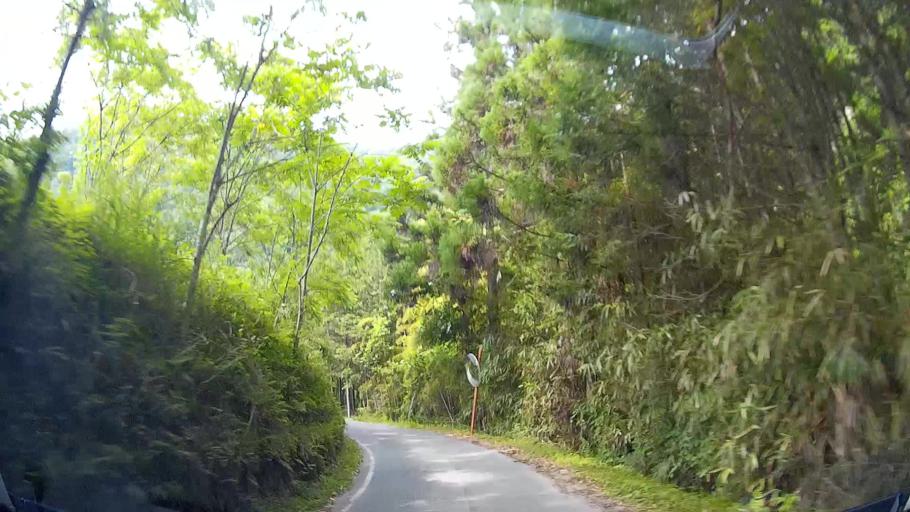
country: JP
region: Nagano
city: Iida
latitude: 35.4881
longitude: 137.9049
